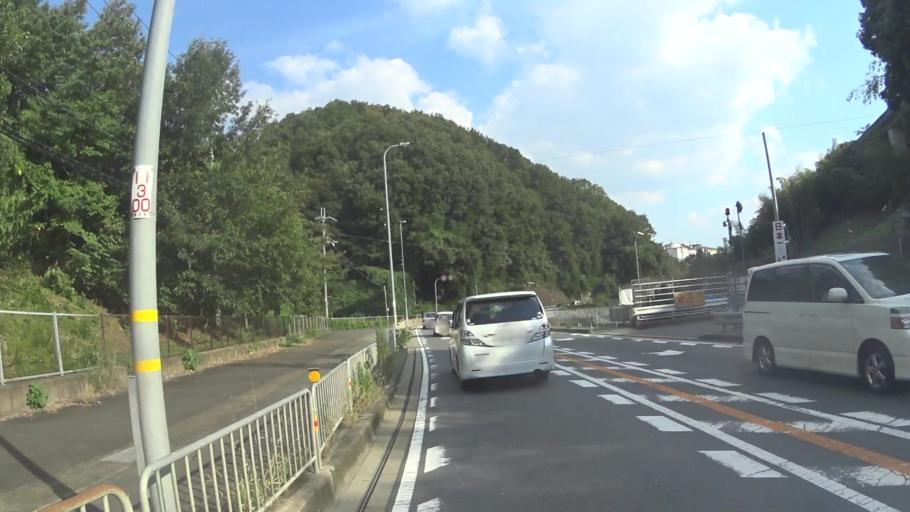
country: JP
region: Kyoto
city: Muko
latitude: 34.9826
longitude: 135.6552
